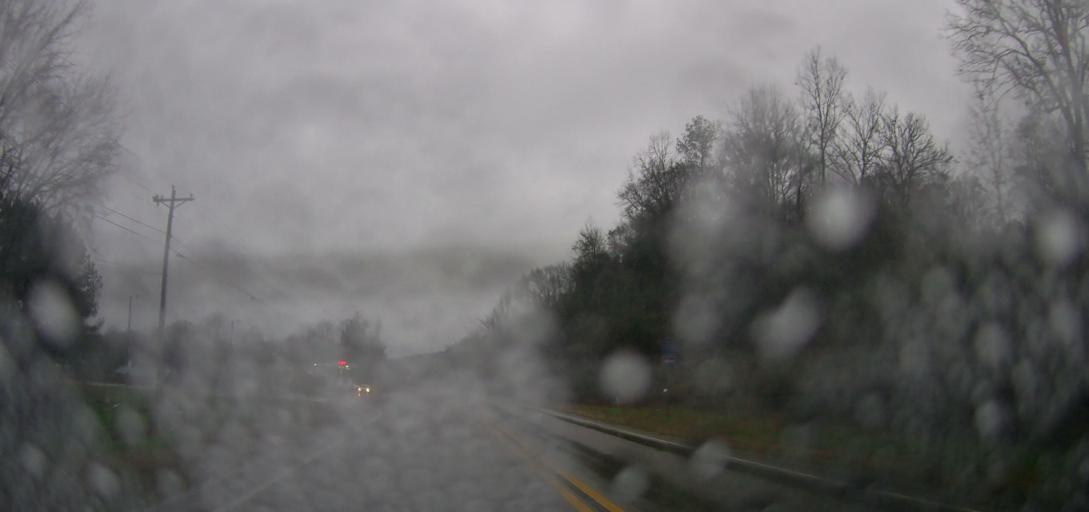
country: US
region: Alabama
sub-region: Autauga County
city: Prattville
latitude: 32.5034
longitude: -86.5851
